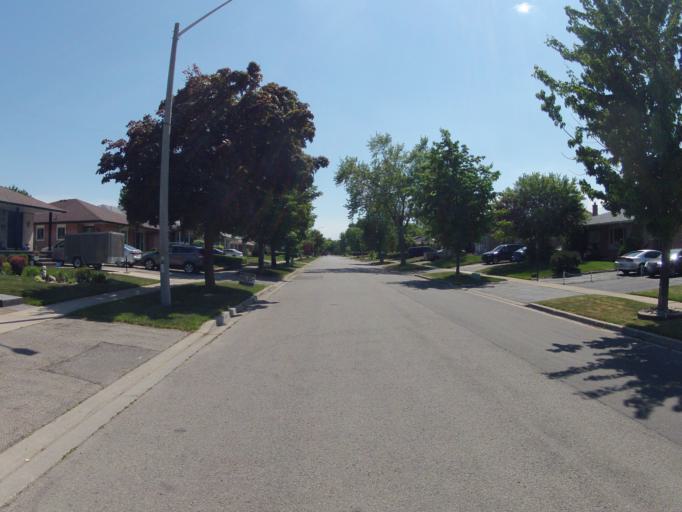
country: CA
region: Ontario
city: Mississauga
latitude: 43.5148
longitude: -79.6512
